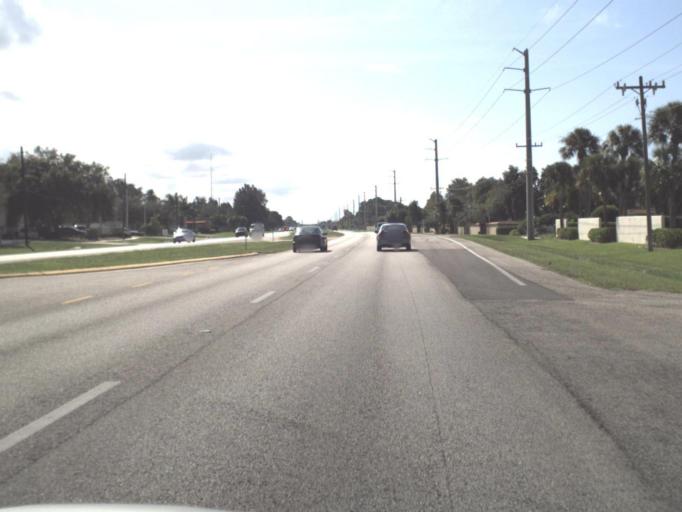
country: US
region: Florida
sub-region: Sarasota County
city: Laurel
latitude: 27.1663
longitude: -82.4763
